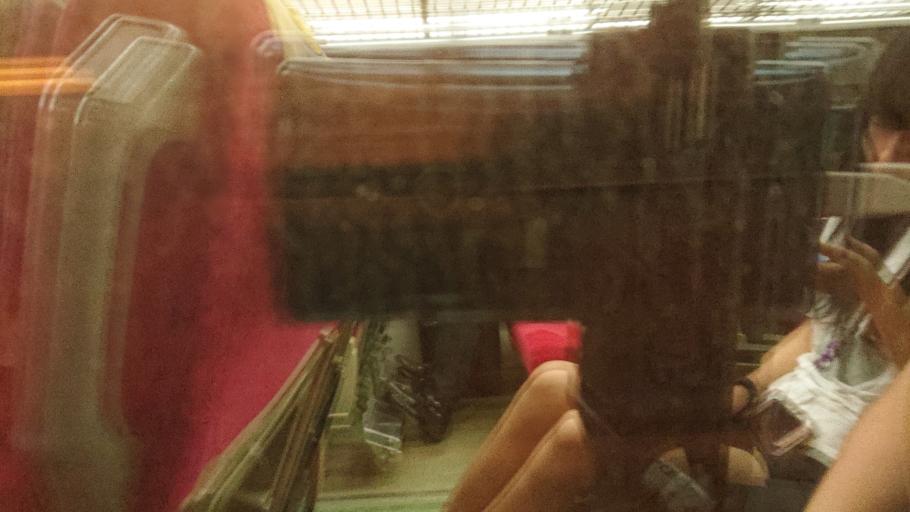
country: TW
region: Taiwan
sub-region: Yilan
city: Yilan
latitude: 24.9184
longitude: 121.8824
